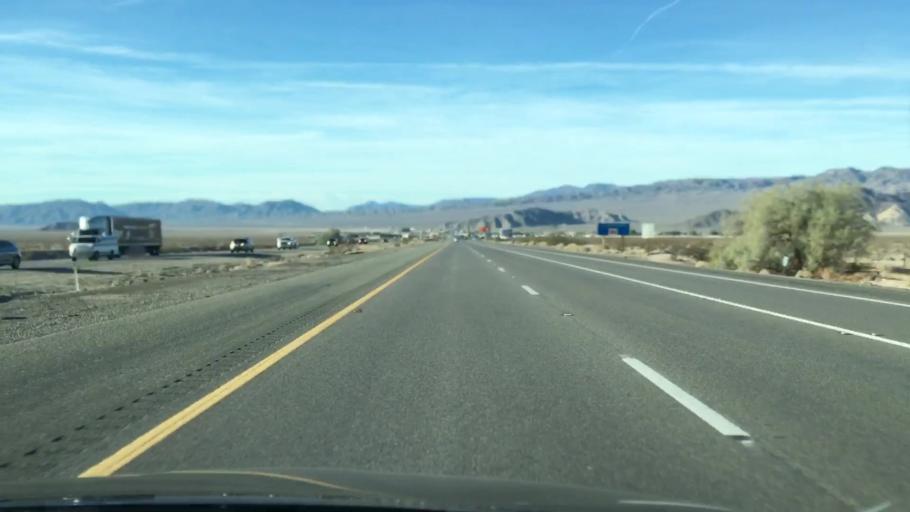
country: US
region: California
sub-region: San Bernardino County
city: Fort Irwin
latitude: 35.2913
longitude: -116.0346
